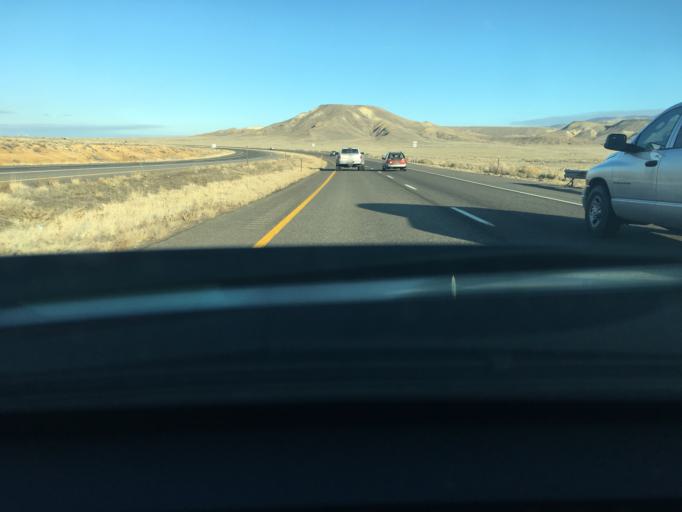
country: US
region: Colorado
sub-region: Delta County
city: Delta
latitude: 38.7732
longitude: -108.2288
